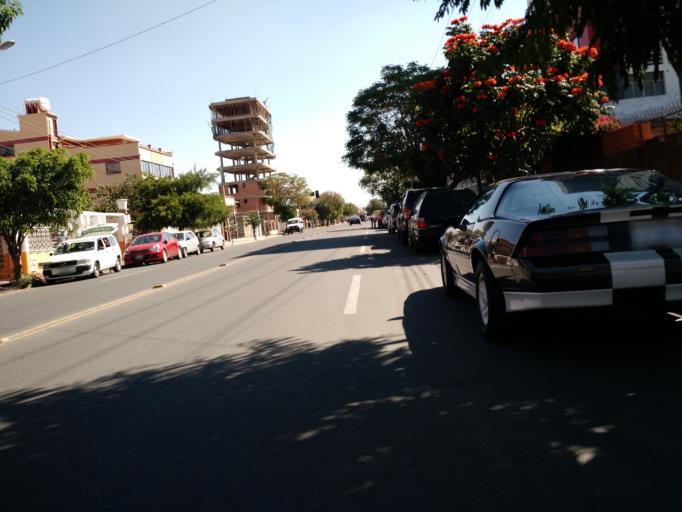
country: BO
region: Cochabamba
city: Cochabamba
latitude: -17.3879
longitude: -66.1726
